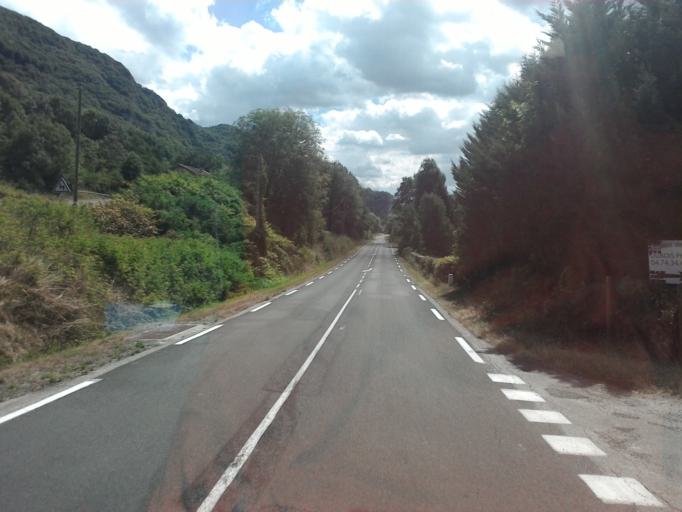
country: FR
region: Rhone-Alpes
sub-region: Departement de l'Ain
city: Lagnieu
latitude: 45.8936
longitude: 5.3585
